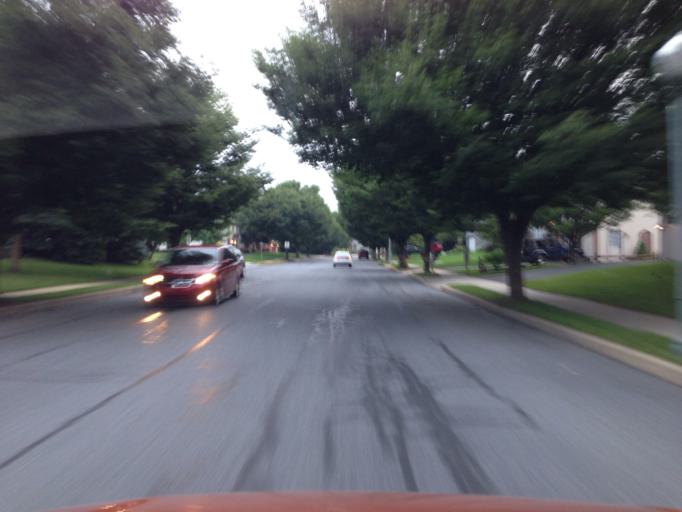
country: US
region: Pennsylvania
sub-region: Lancaster County
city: Lititz
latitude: 40.1458
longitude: -76.2987
